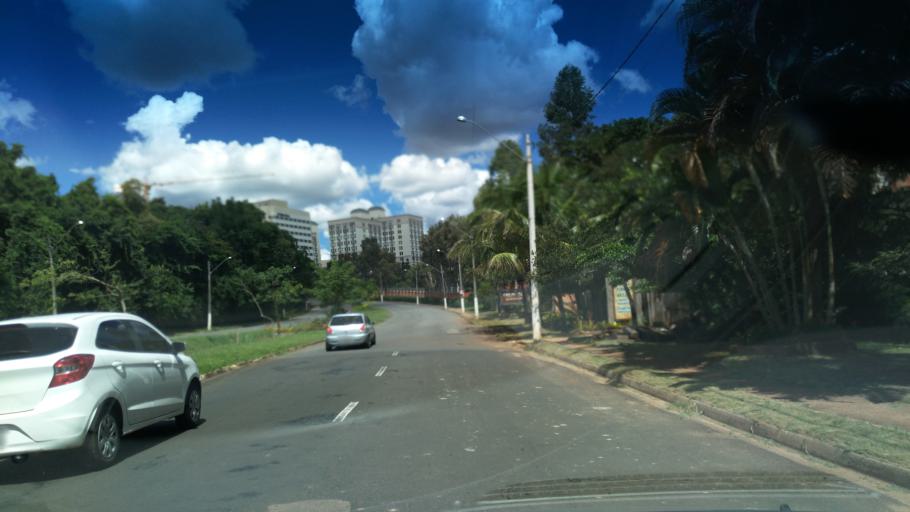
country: BR
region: Sao Paulo
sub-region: Valinhos
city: Valinhos
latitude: -22.9776
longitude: -47.0151
